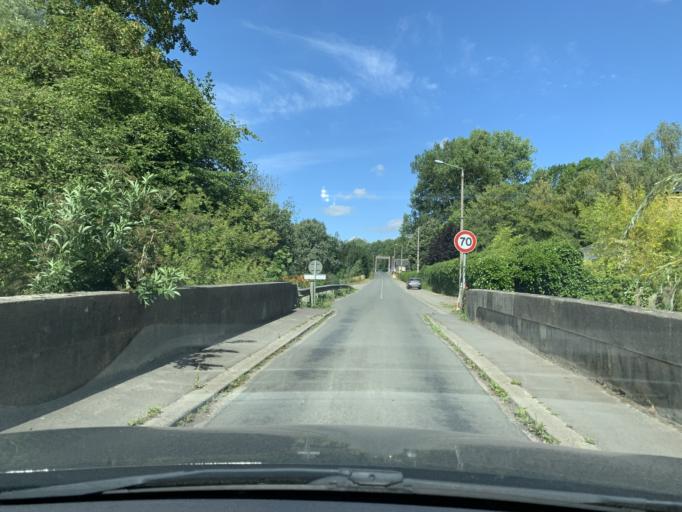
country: FR
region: Nord-Pas-de-Calais
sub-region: Departement du Nord
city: Proville
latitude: 50.1540
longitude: 3.1878
